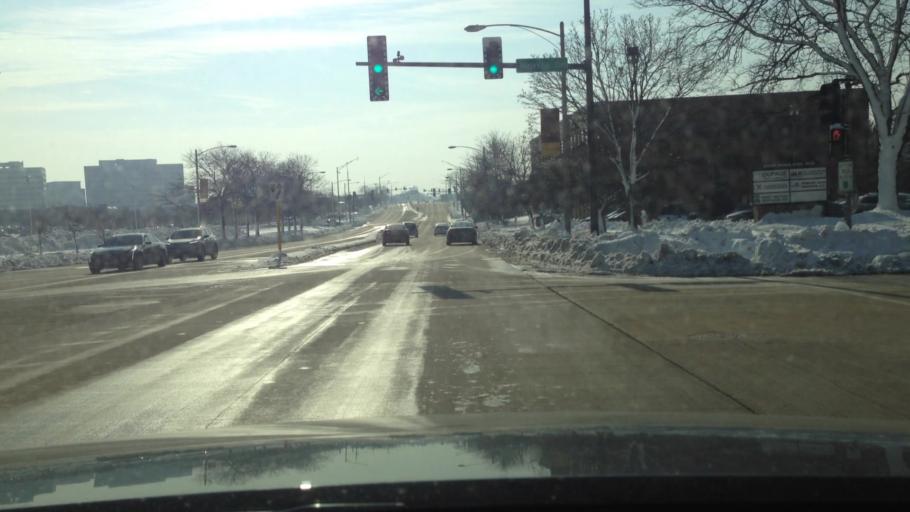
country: US
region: Illinois
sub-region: DuPage County
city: Downers Grove
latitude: 41.8418
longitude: -88.0115
